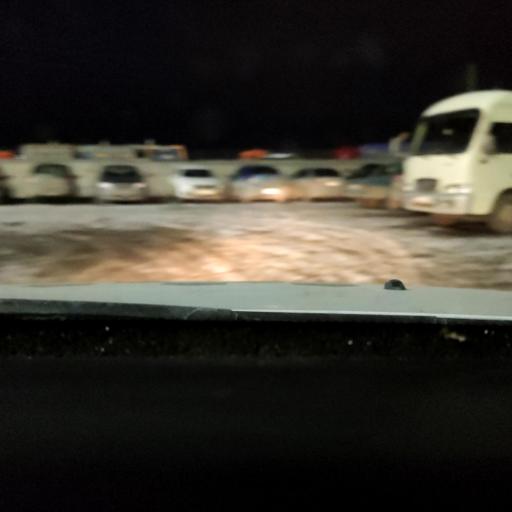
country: RU
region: Perm
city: Kondratovo
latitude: 57.9341
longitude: 56.1468
